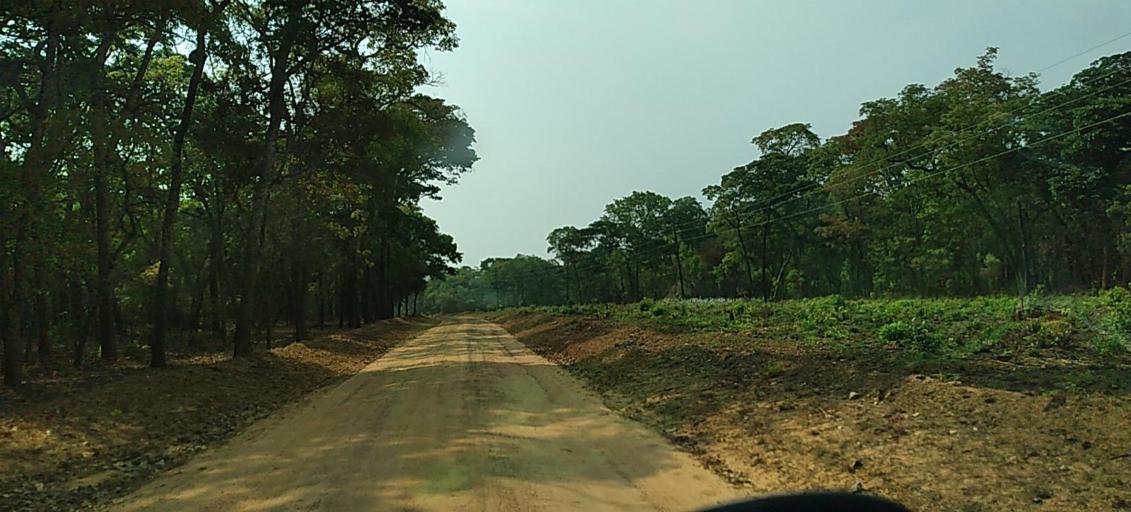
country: ZM
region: North-Western
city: Solwezi
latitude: -12.6877
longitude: 26.3971
